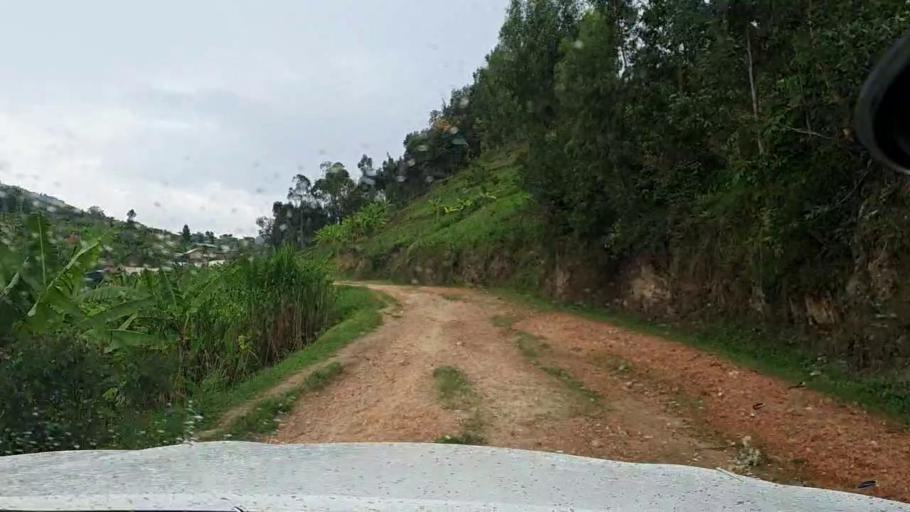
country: RW
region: Western Province
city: Kibuye
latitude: -2.0762
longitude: 29.4393
